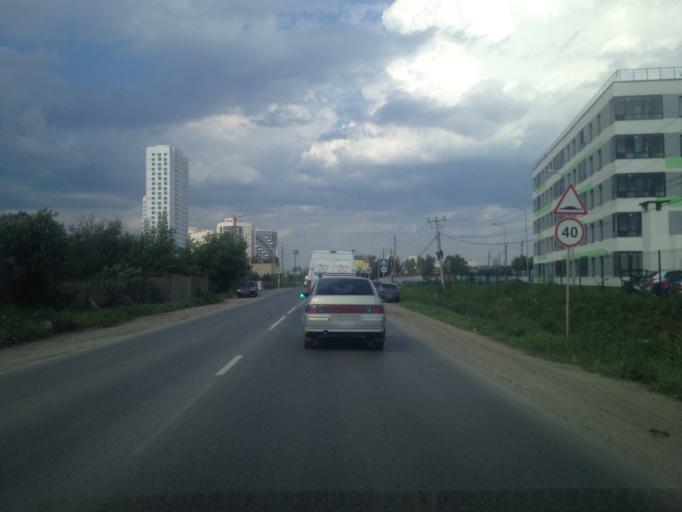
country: RU
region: Sverdlovsk
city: Shirokaya Rechka
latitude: 56.7956
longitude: 60.4901
